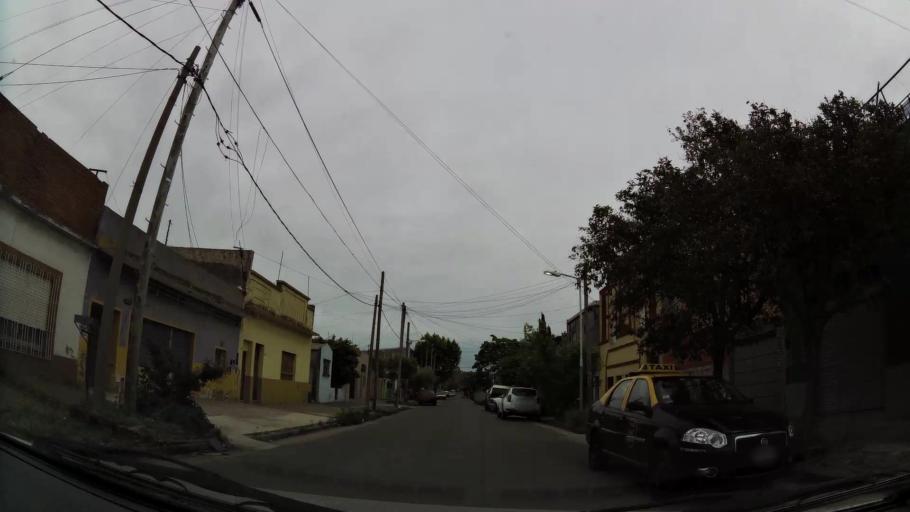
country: AR
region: Buenos Aires
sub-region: Partido de Avellaneda
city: Avellaneda
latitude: -34.6529
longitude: -58.3439
